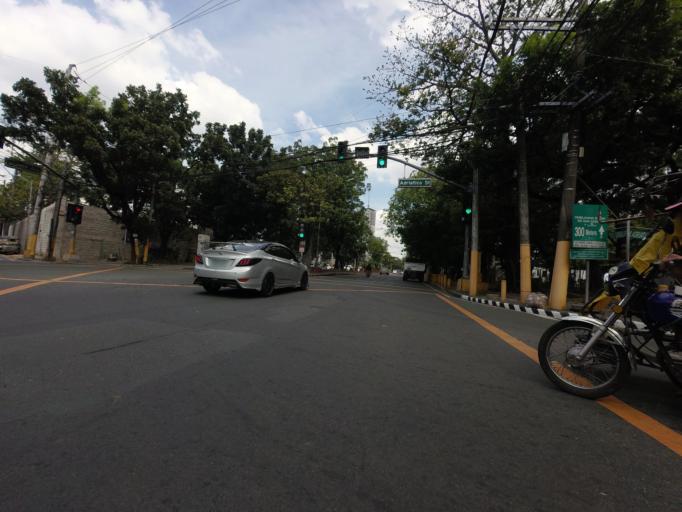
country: PH
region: Metro Manila
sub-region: City of Manila
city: Port Area
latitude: 14.5662
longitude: 120.9884
